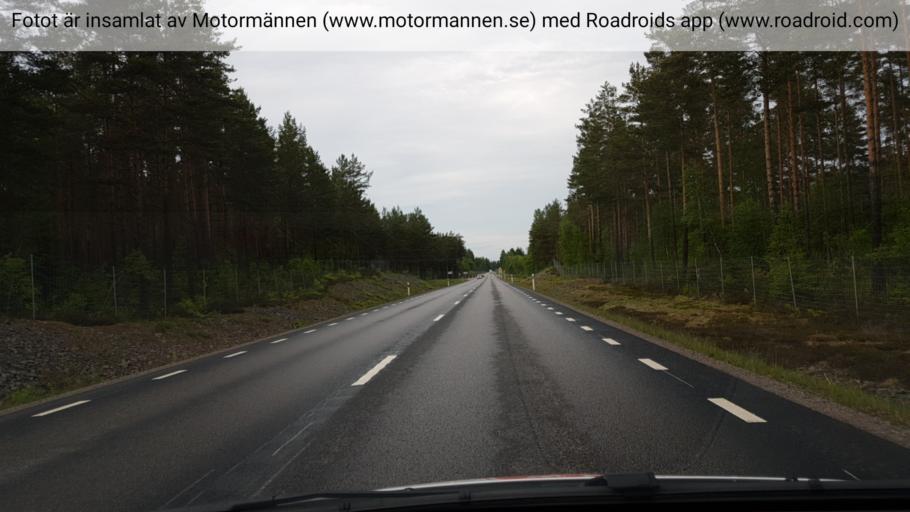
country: SE
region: Kalmar
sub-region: Vimmerby Kommun
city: Vimmerby
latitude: 57.6287
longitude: 15.8390
